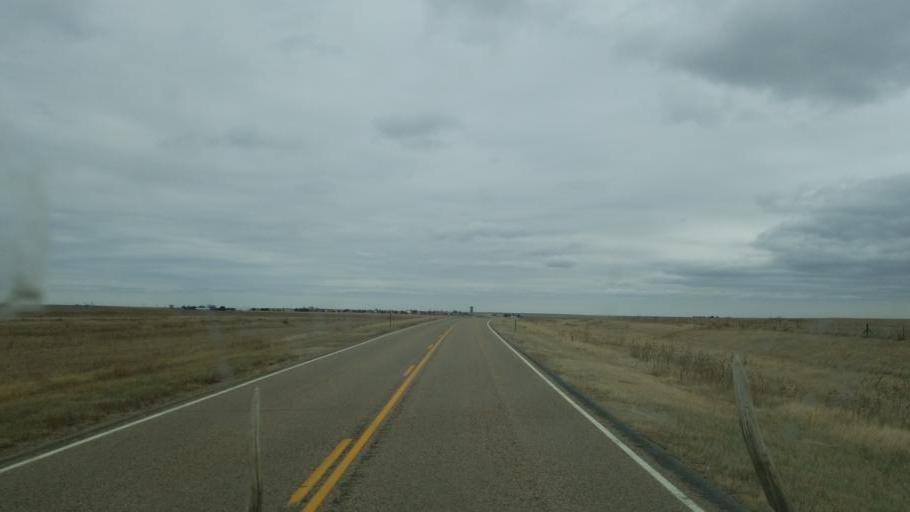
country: US
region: Colorado
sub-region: Cheyenne County
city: Cheyenne Wells
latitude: 38.8521
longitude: -102.2007
